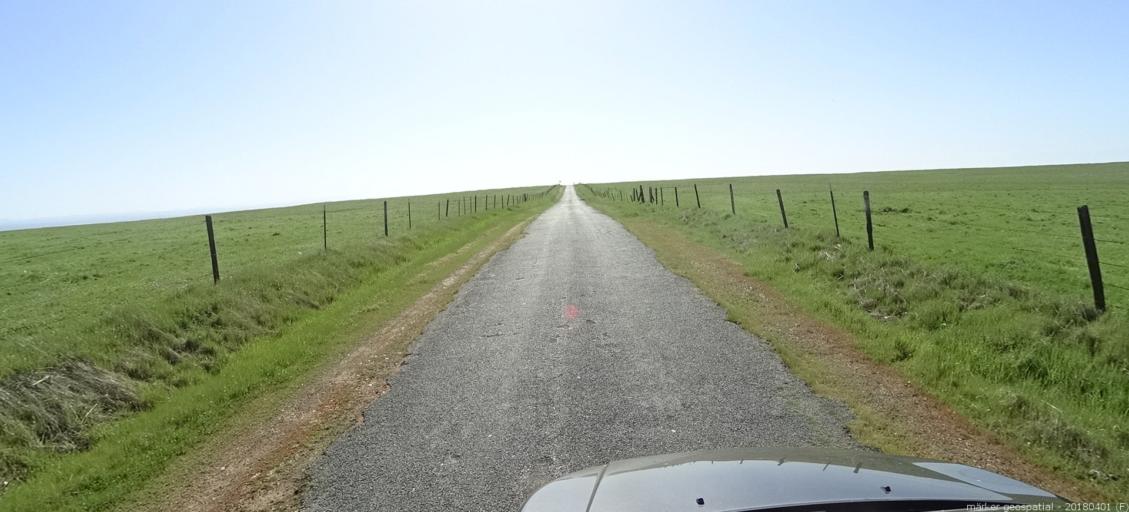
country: US
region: California
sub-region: Sacramento County
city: Rancho Murieta
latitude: 38.4585
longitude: -121.1067
